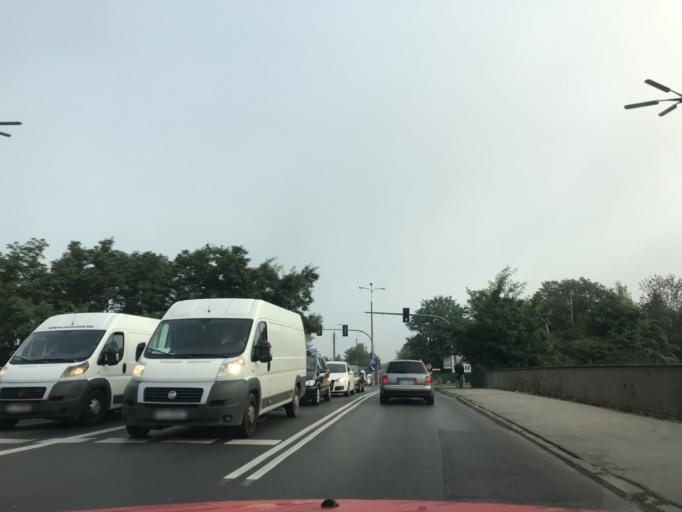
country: PL
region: Greater Poland Voivodeship
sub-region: Powiat poznanski
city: Baranowo
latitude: 52.4318
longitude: 16.8084
